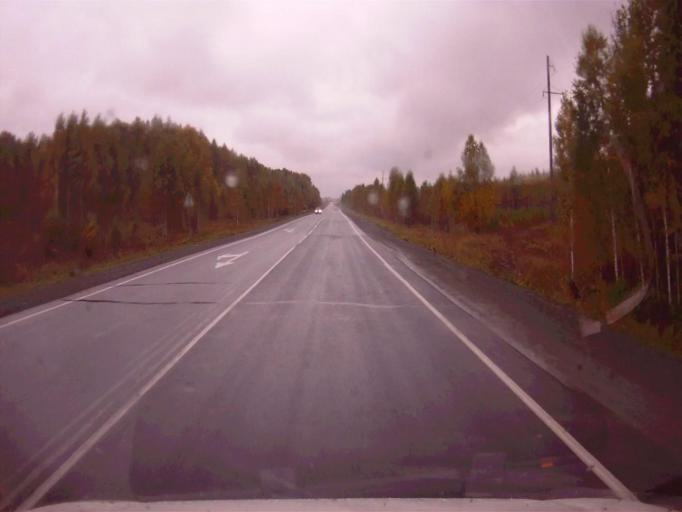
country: RU
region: Chelyabinsk
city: Novogornyy
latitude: 55.4894
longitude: 60.6853
